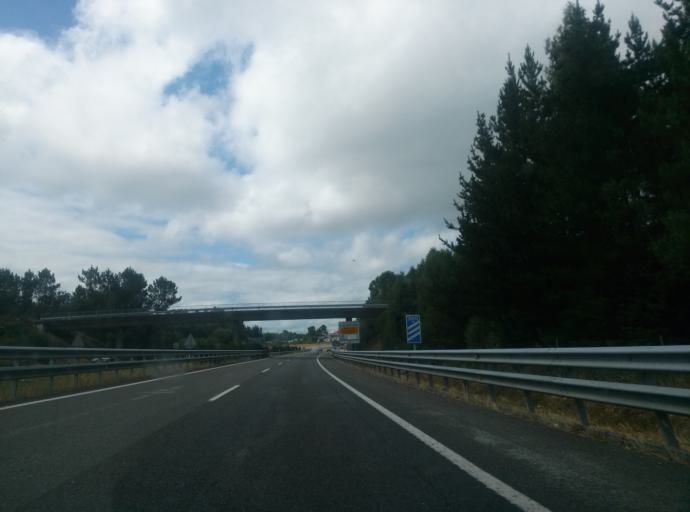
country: ES
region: Galicia
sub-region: Provincia de Lugo
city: Outeiro de Rei
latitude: 43.1001
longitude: -7.5988
